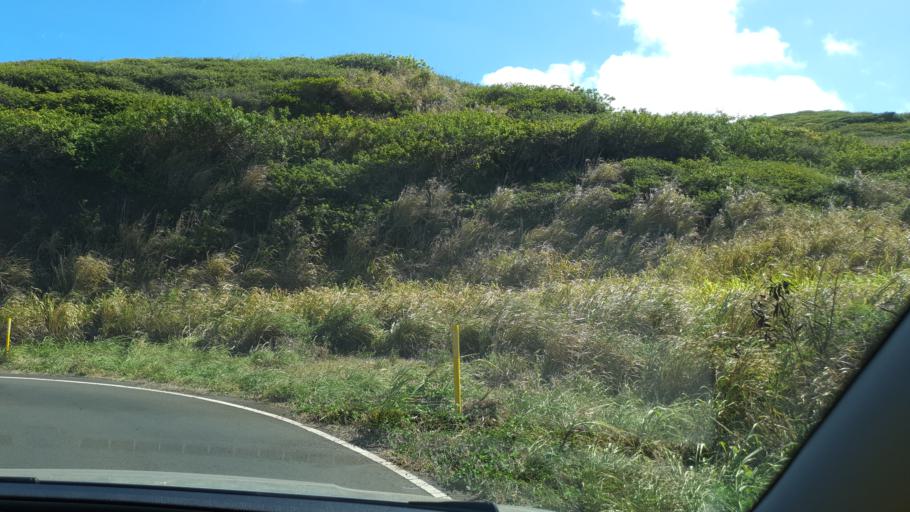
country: US
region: Hawaii
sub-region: Maui County
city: Napili-Honokowai
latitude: 21.0122
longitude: -156.5716
